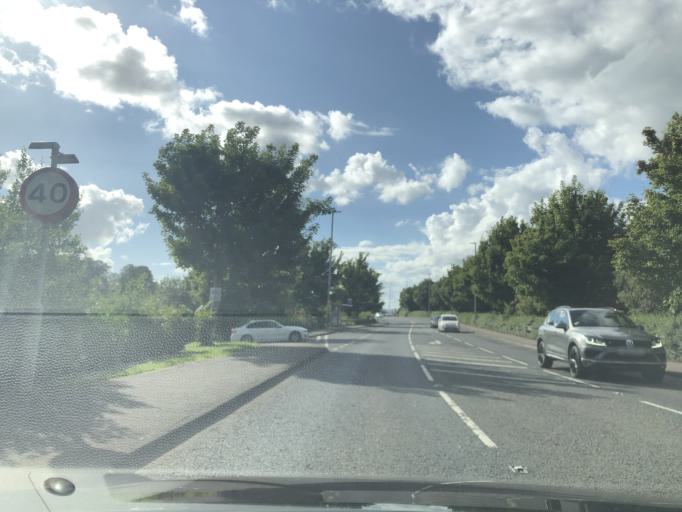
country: GB
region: Northern Ireland
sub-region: Castlereagh District
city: Dundonald
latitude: 54.5876
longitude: -5.8160
